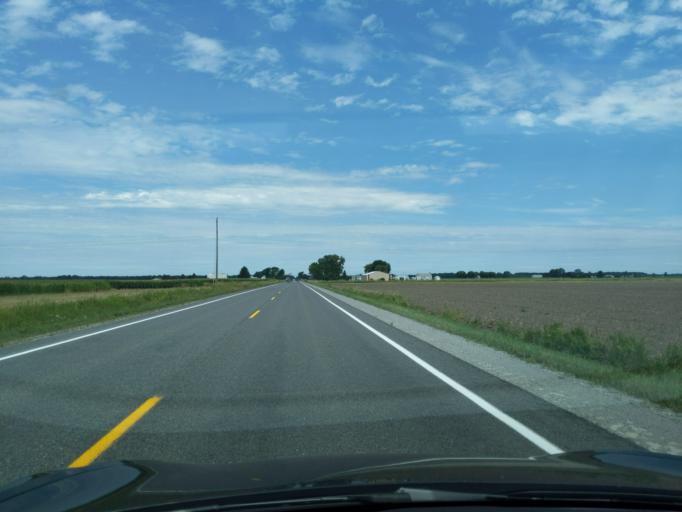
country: US
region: Michigan
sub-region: Gratiot County
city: Breckenridge
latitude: 43.4867
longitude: -84.3697
